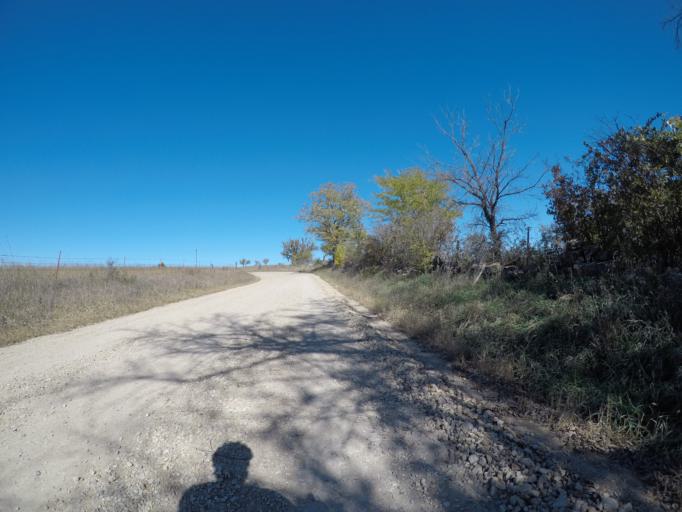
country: US
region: Kansas
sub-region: Wabaunsee County
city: Alma
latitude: 38.9742
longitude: -96.3627
